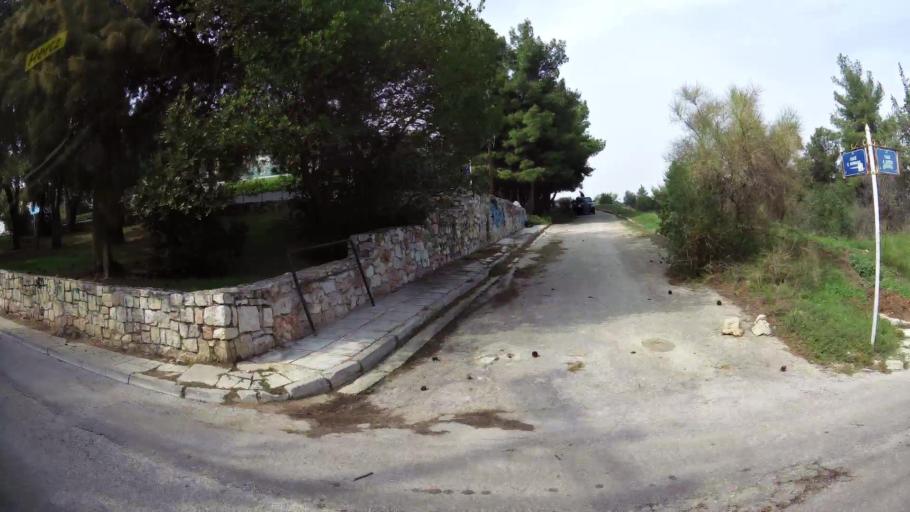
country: GR
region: Attica
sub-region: Nomarchia Athinas
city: Psychiko
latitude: 38.0166
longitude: 23.7664
